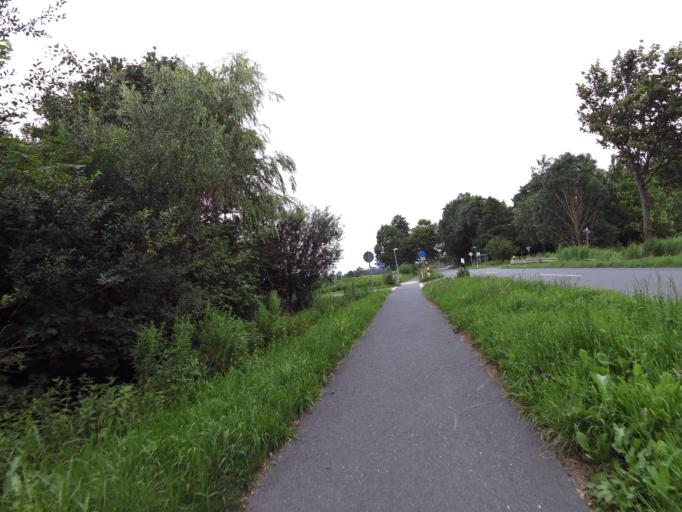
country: DE
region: Lower Saxony
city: Dorum
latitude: 53.7004
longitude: 8.5587
